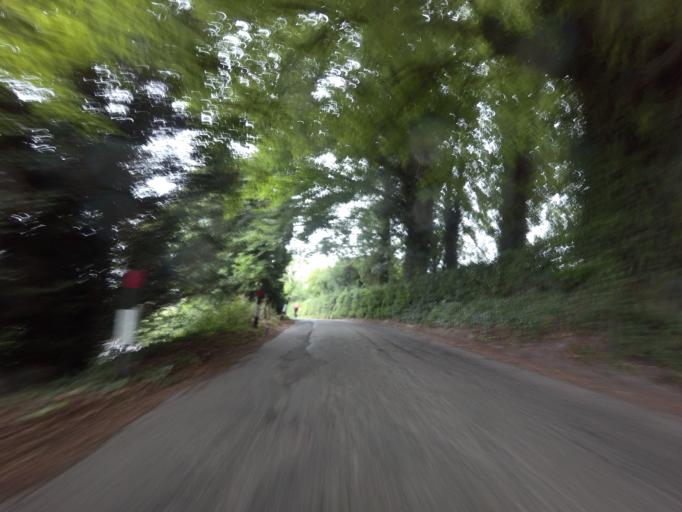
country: GB
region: England
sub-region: Kent
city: Kemsing
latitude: 51.3112
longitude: 0.2545
